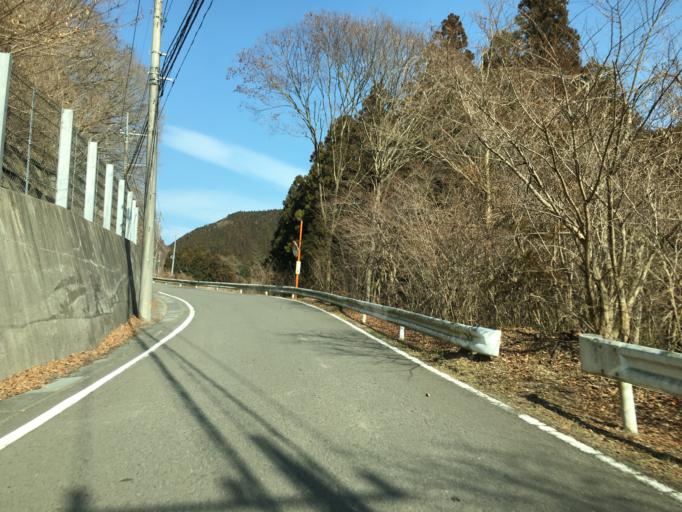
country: JP
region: Ibaraki
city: Daigo
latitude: 36.8000
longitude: 140.4921
